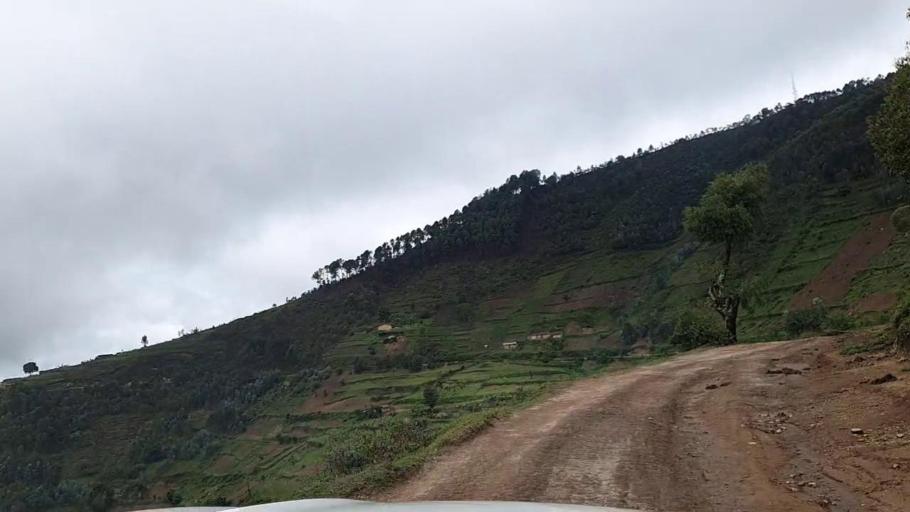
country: RW
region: Southern Province
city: Gikongoro
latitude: -2.3619
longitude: 29.4961
